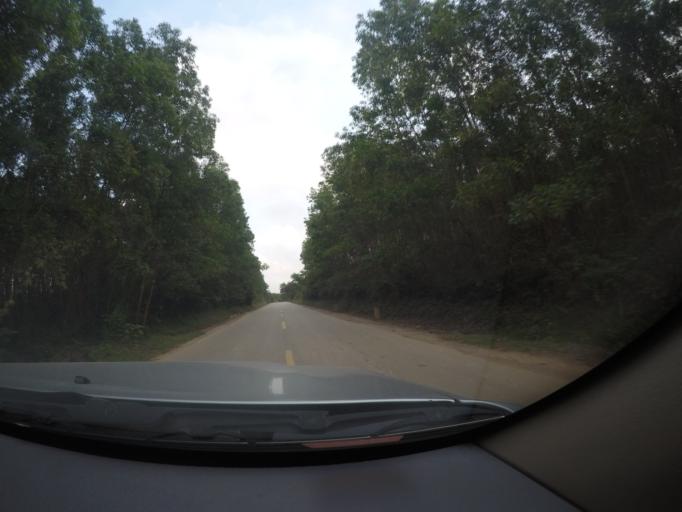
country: VN
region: Quang Binh
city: Kien Giang
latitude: 17.1167
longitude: 106.8066
